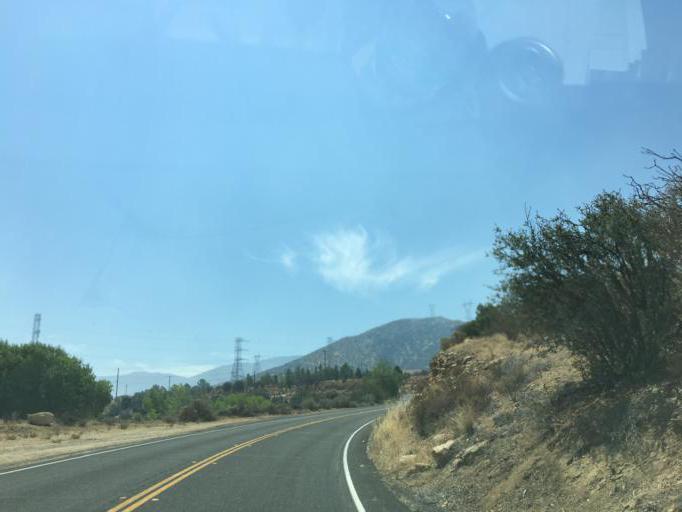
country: US
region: California
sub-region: Los Angeles County
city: Acton
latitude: 34.4372
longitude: -118.1407
